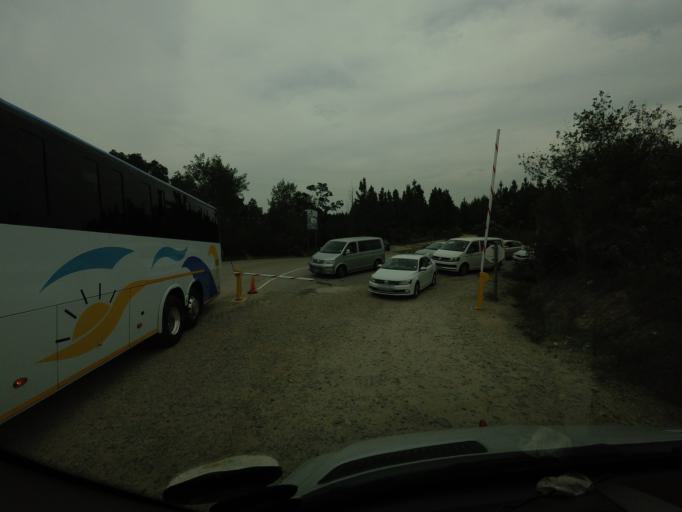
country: ZA
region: Eastern Cape
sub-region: Cacadu District Municipality
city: Kareedouw
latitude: -34.0106
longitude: 23.8688
